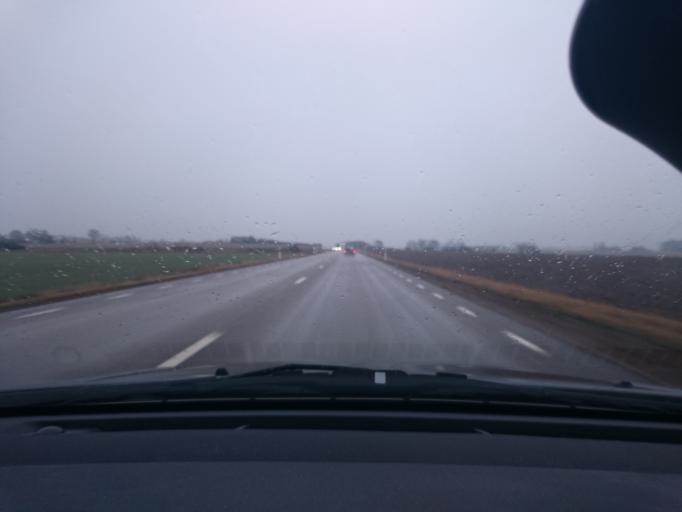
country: SE
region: Skane
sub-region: Bastads Kommun
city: Forslov
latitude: 56.3296
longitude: 12.8204
